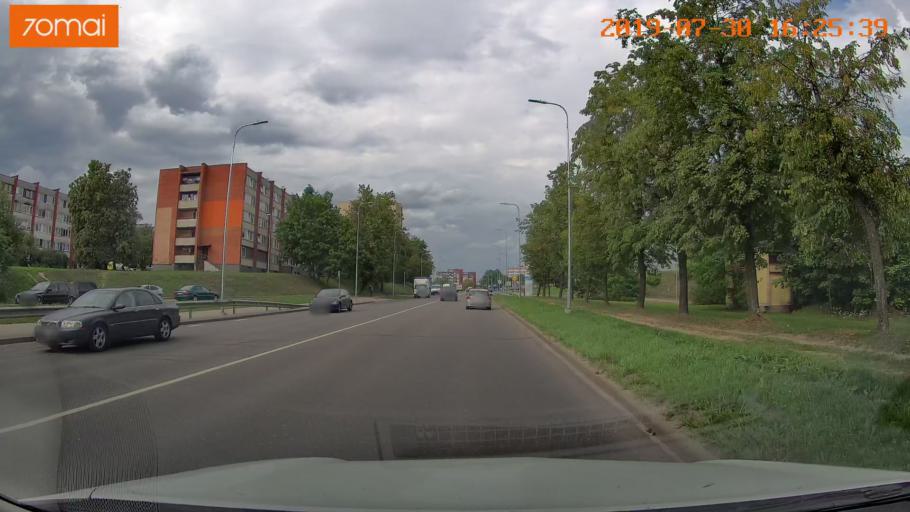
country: LT
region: Vilnius County
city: Naujamiestis
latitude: 54.6589
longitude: 25.2730
